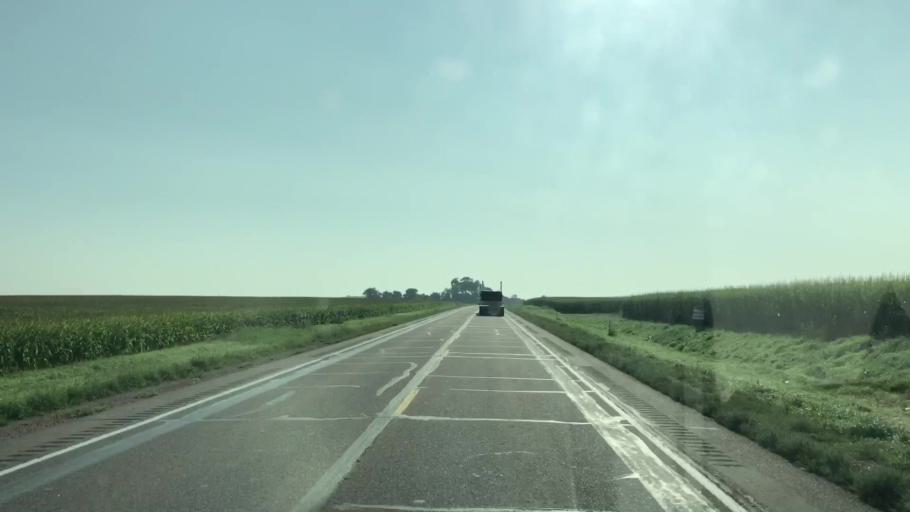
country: US
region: Iowa
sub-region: O'Brien County
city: Sheldon
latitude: 43.1863
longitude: -95.9764
